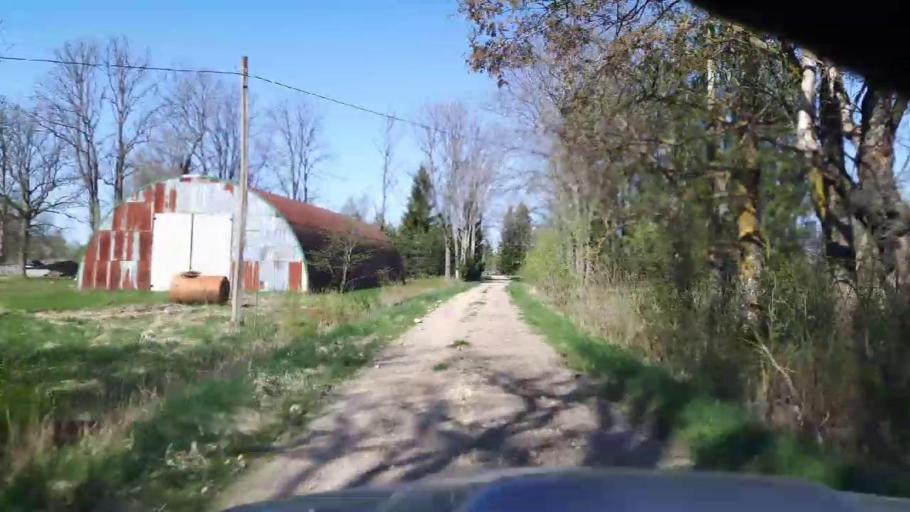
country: EE
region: Paernumaa
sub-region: Tootsi vald
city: Tootsi
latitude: 58.4628
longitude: 24.7847
